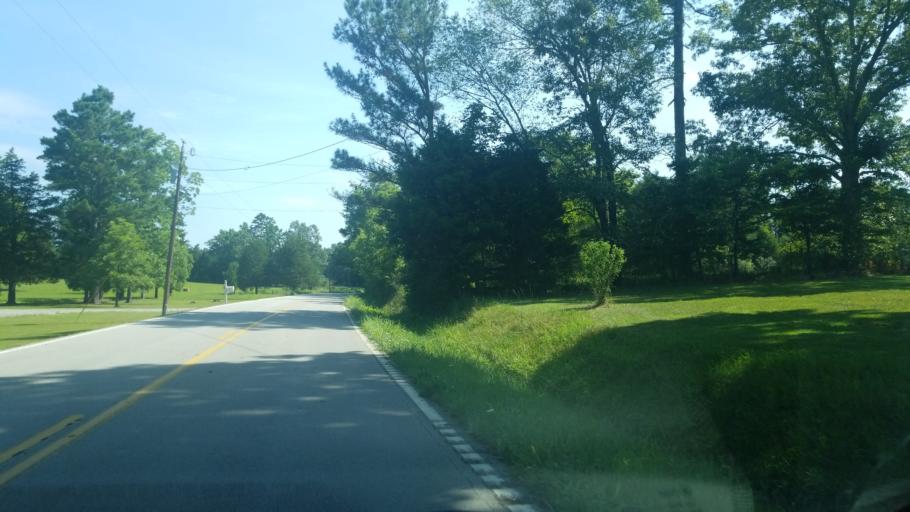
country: US
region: Tennessee
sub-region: Hamilton County
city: Sale Creek
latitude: 35.3380
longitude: -85.0053
